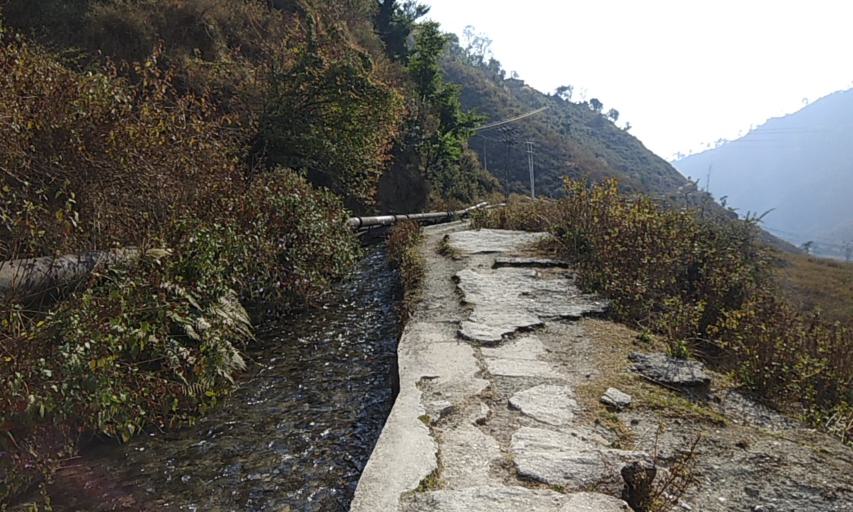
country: IN
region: Himachal Pradesh
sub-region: Kangra
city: Palampur
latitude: 32.1475
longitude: 76.5432
